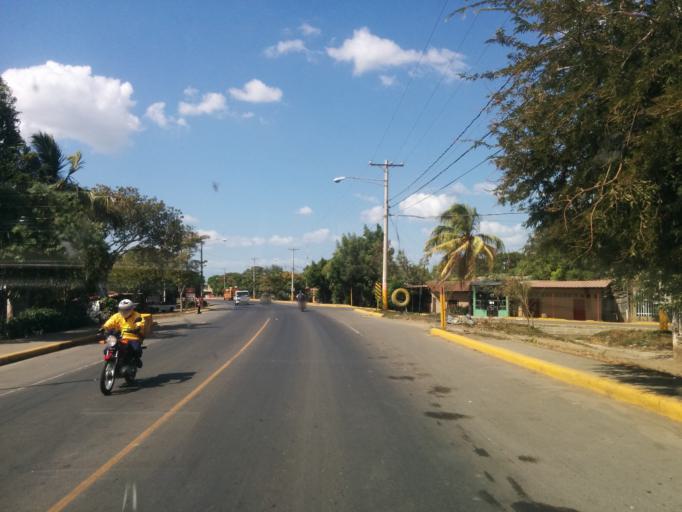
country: NI
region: Managua
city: Tipitapa
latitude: 12.1924
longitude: -86.0980
